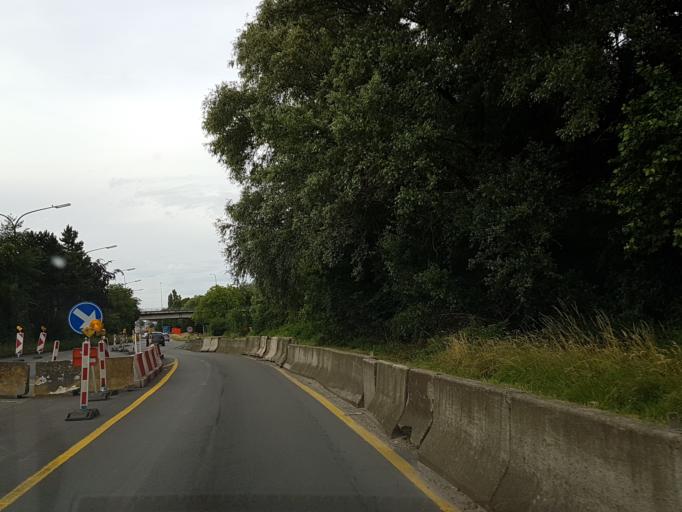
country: BE
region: Flanders
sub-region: Provincie Vlaams-Brabant
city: Kraainem
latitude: 50.8616
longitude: 4.4511
